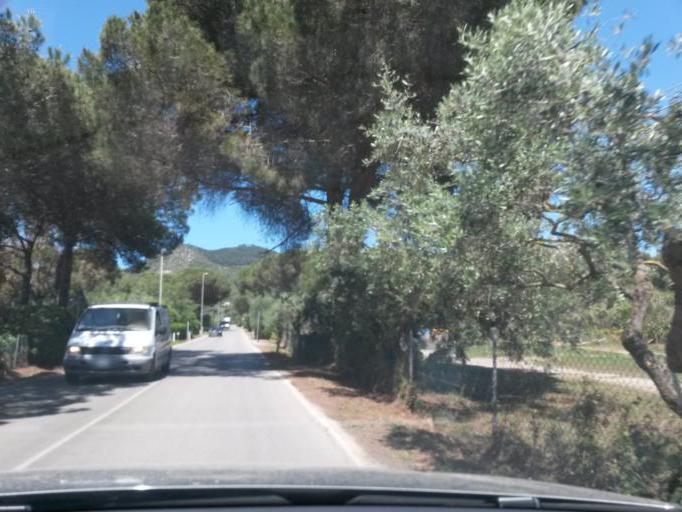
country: IT
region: Tuscany
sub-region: Provincia di Livorno
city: Portoferraio
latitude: 42.7607
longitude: 10.3164
